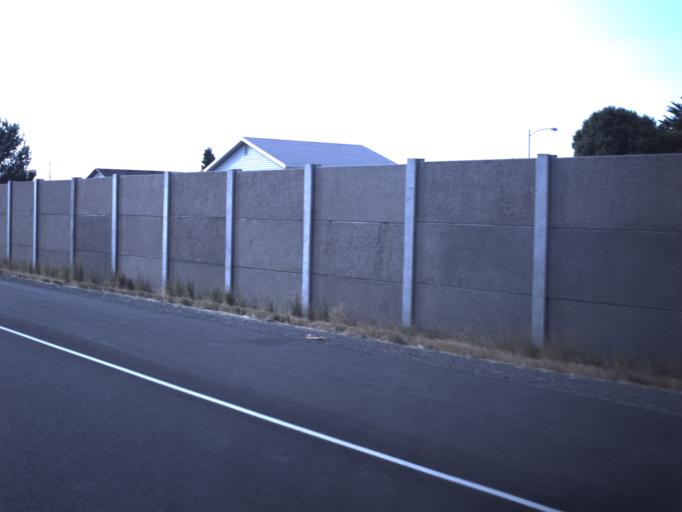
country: US
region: Utah
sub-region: Salt Lake County
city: Midvale
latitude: 40.6364
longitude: -111.9129
